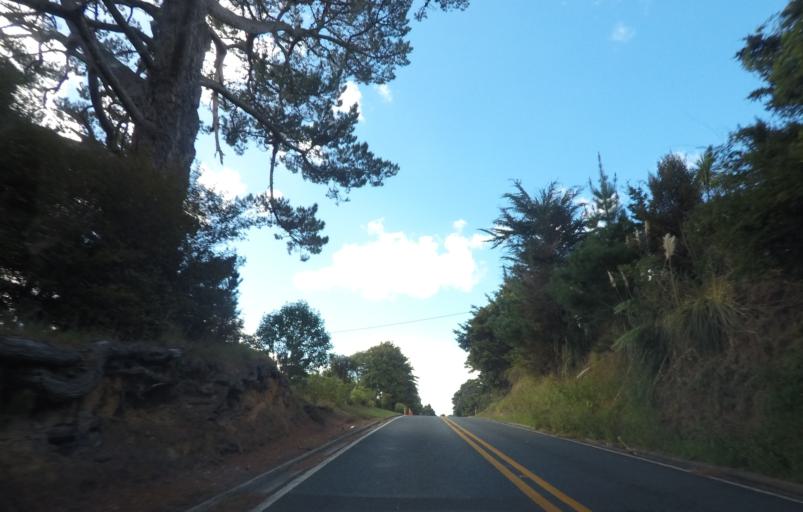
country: NZ
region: Auckland
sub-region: Auckland
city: Parakai
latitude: -36.6317
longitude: 174.5534
